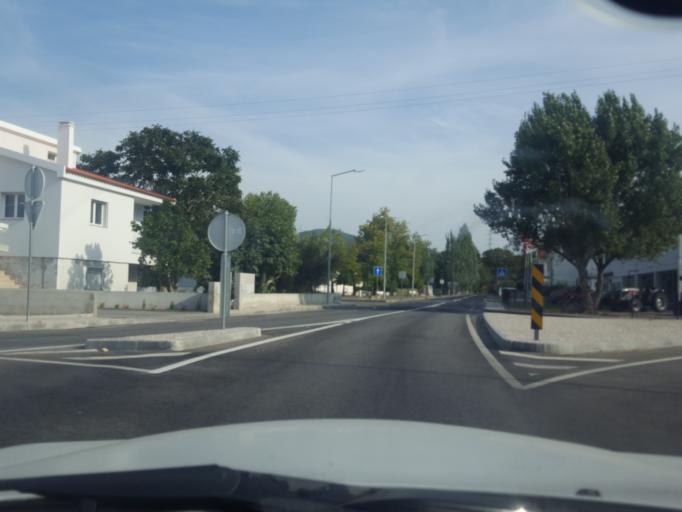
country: PT
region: Leiria
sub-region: Leiria
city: Leiria
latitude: 39.6999
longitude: -8.7890
